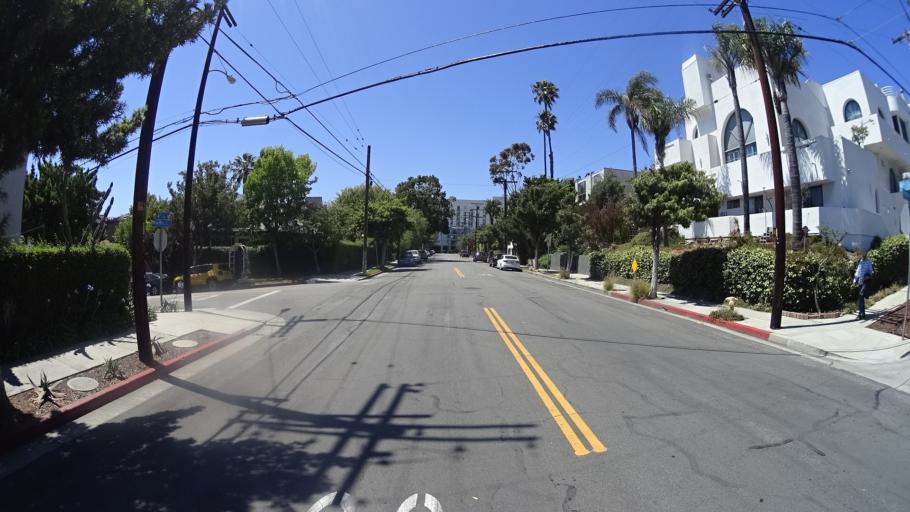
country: US
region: California
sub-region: Los Angeles County
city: Santa Monica
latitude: 34.0087
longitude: -118.4833
